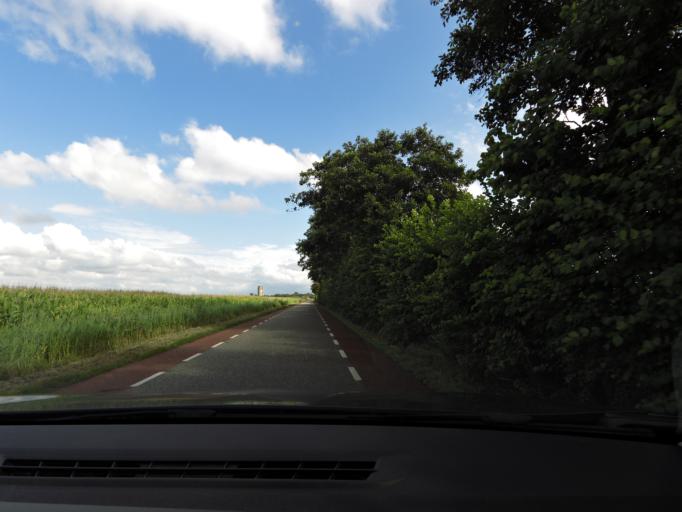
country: NL
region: South Holland
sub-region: Gemeente Goeree-Overflakkee
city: Goedereede
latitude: 51.8238
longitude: 3.9629
